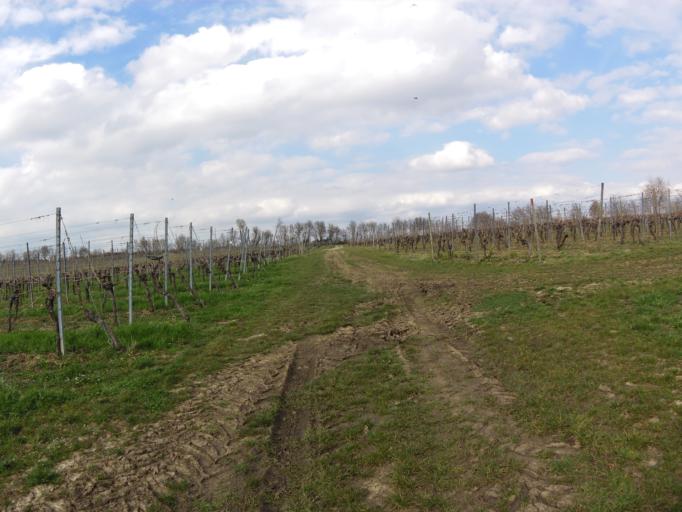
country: DE
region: Bavaria
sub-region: Regierungsbezirk Unterfranken
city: Buchbrunn
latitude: 49.7368
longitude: 10.1235
